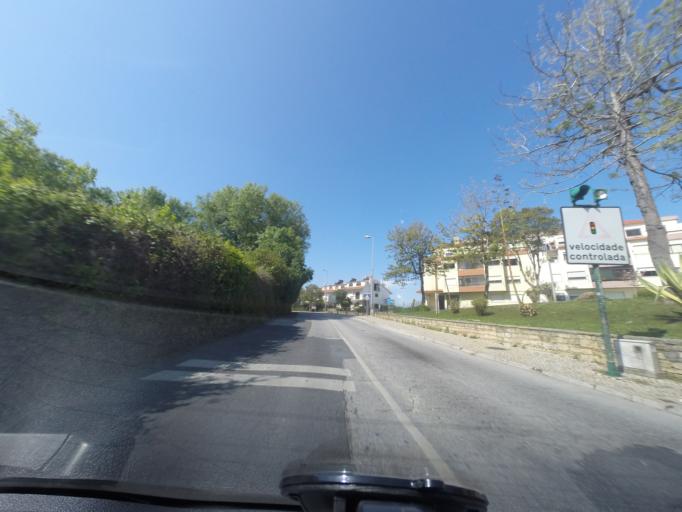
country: PT
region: Lisbon
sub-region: Sintra
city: Sintra
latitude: 38.8062
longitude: -9.3797
